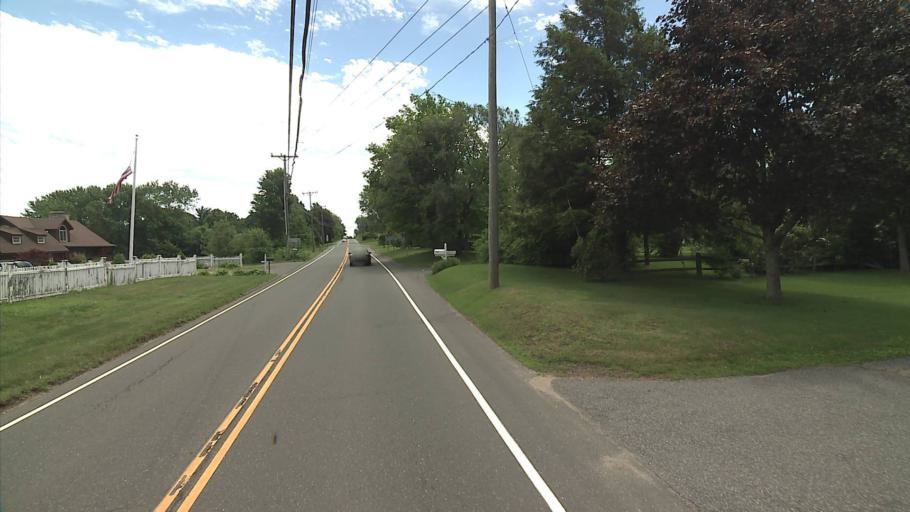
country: US
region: Connecticut
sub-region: Litchfield County
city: Watertown
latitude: 41.6466
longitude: -73.1495
